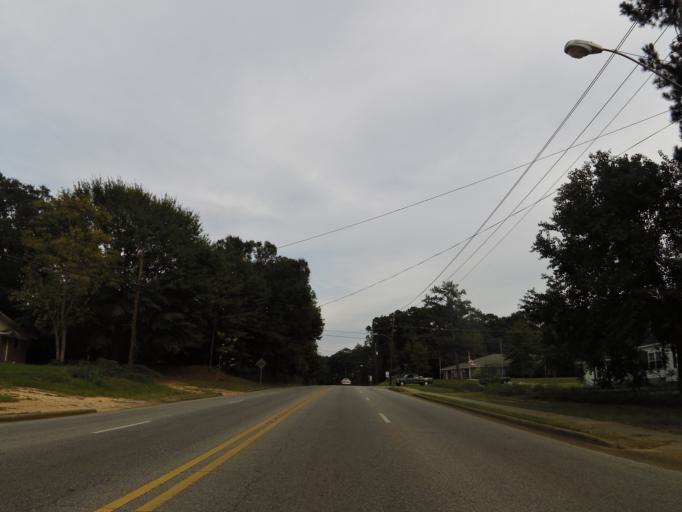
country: US
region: Alabama
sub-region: Monroe County
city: Monroeville
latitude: 31.5265
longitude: -87.3364
